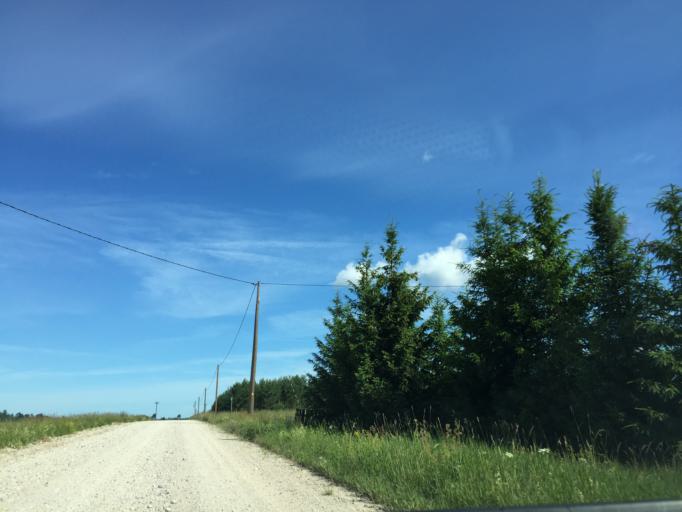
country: LV
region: Dundaga
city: Dundaga
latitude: 57.3438
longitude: 22.0281
